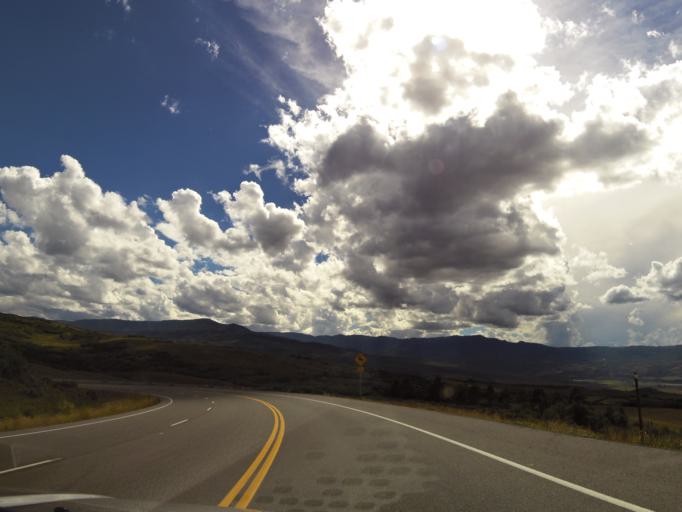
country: US
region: Colorado
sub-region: Hinsdale County
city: Lake City
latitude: 38.3966
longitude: -107.4539
